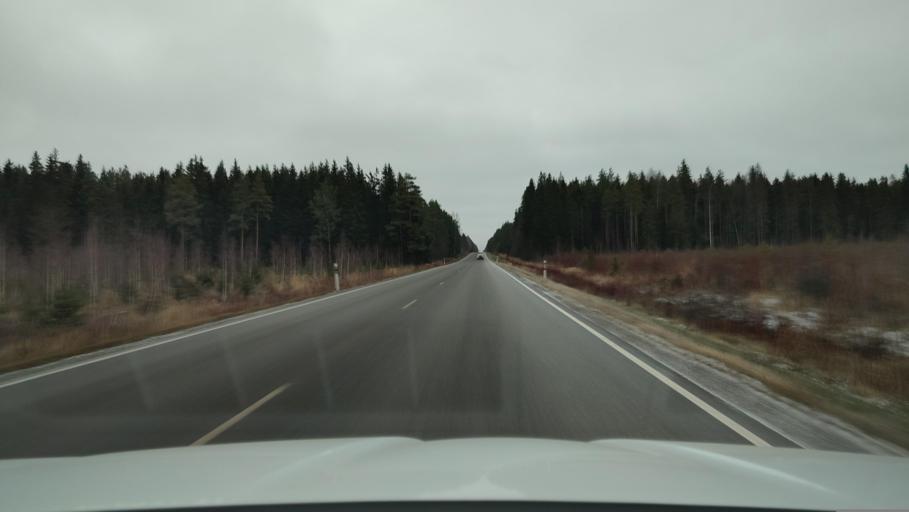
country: FI
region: Ostrobothnia
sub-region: Sydosterbotten
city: Naerpes
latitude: 62.5562
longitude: 21.4765
